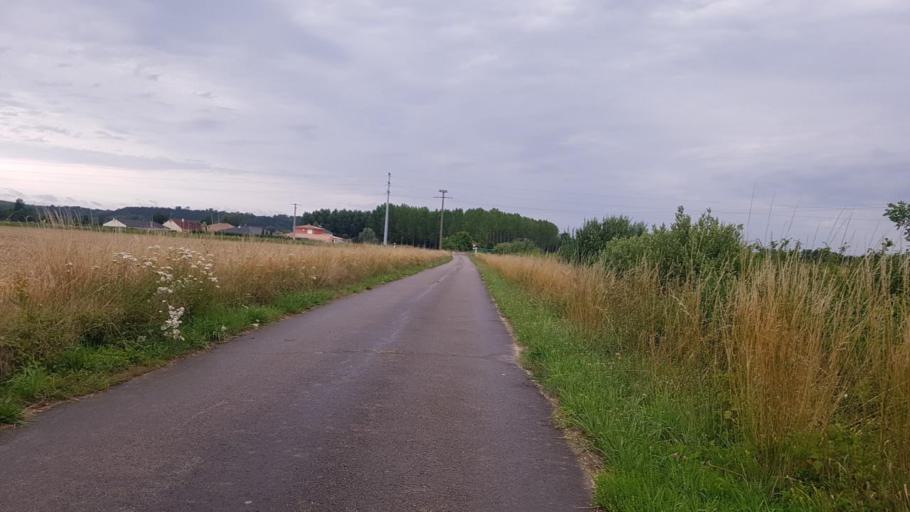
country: FR
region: Champagne-Ardenne
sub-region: Departement de la Marne
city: Vitry-le-Francois
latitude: 48.7404
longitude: 4.6595
